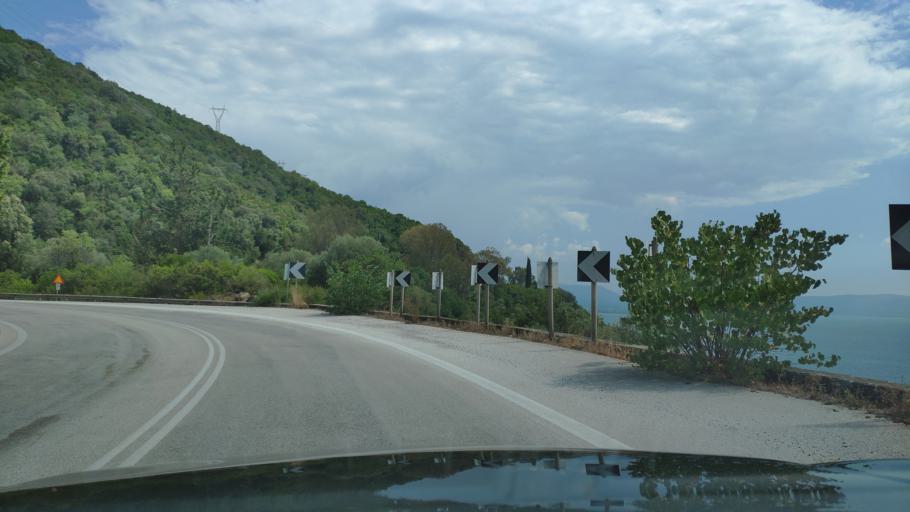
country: GR
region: West Greece
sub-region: Nomos Aitolias kai Akarnanias
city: Menidi
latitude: 39.0166
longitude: 21.1393
